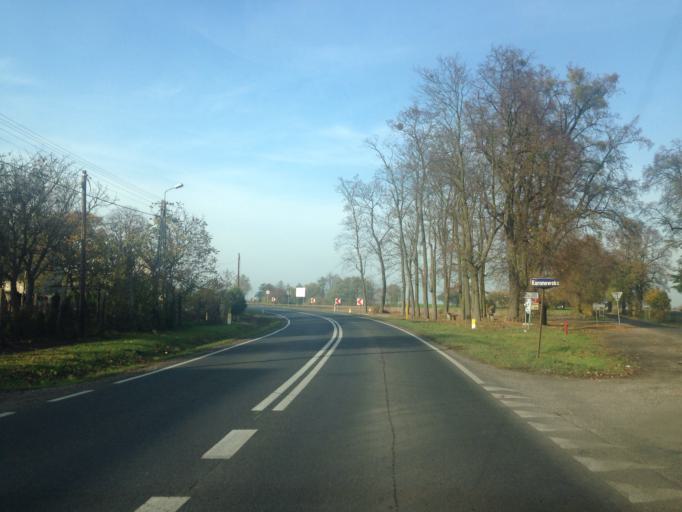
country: PL
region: Kujawsko-Pomorskie
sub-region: Powiat swiecki
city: Pruszcz
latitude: 53.2986
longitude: 18.1143
